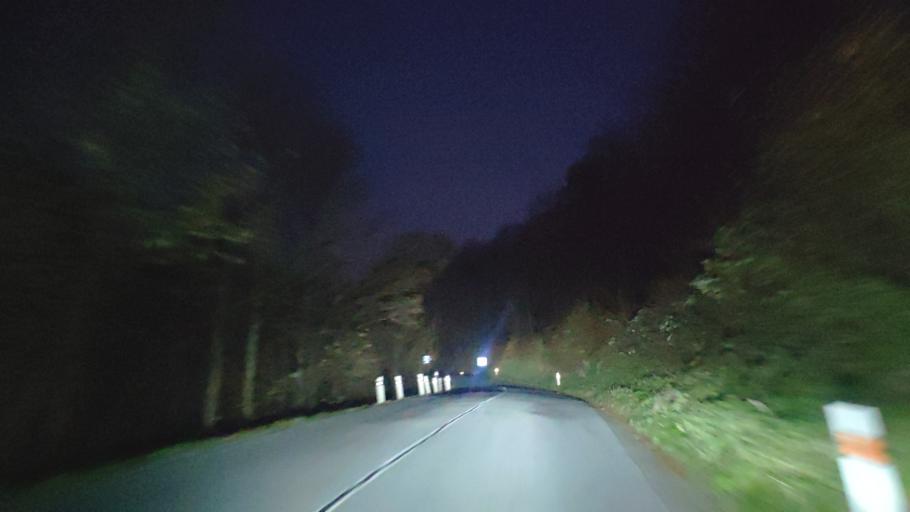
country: SK
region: Kosicky
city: Gelnica
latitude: 48.9024
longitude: 21.0235
